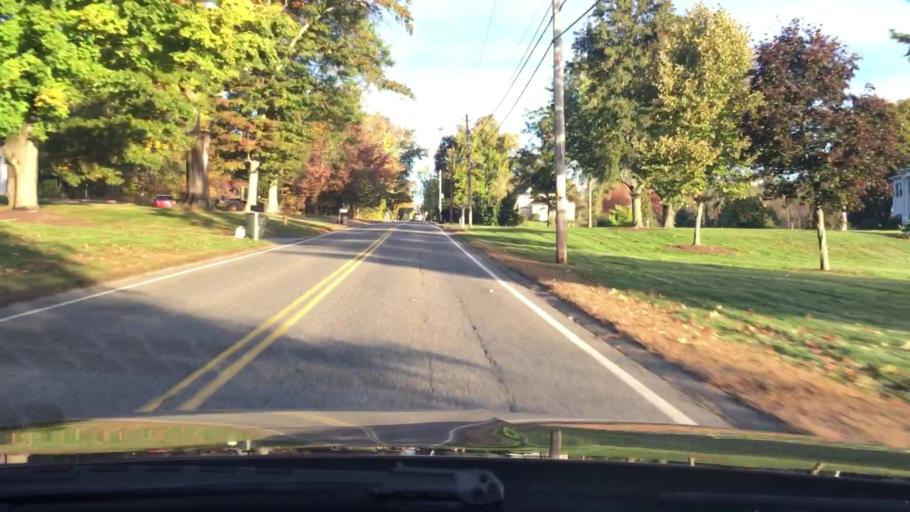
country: US
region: Massachusetts
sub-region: Hampden County
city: East Longmeadow
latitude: 42.0398
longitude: -72.4979
